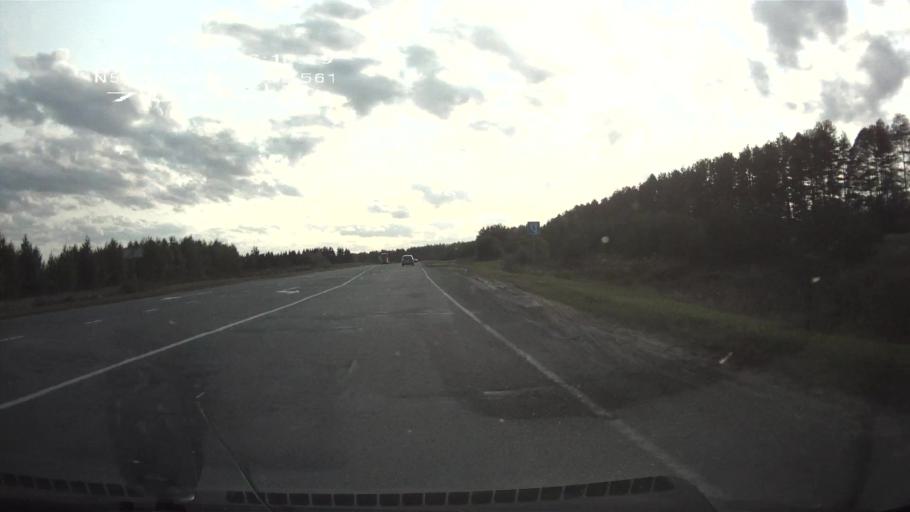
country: RU
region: Mariy-El
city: Kuzhener
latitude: 56.8154
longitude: 48.7121
